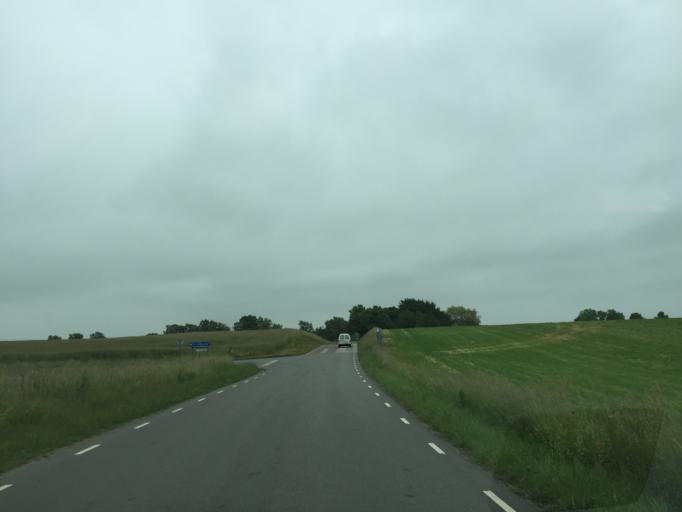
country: SE
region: Skane
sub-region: Ystads Kommun
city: Kopingebro
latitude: 55.4467
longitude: 14.0280
